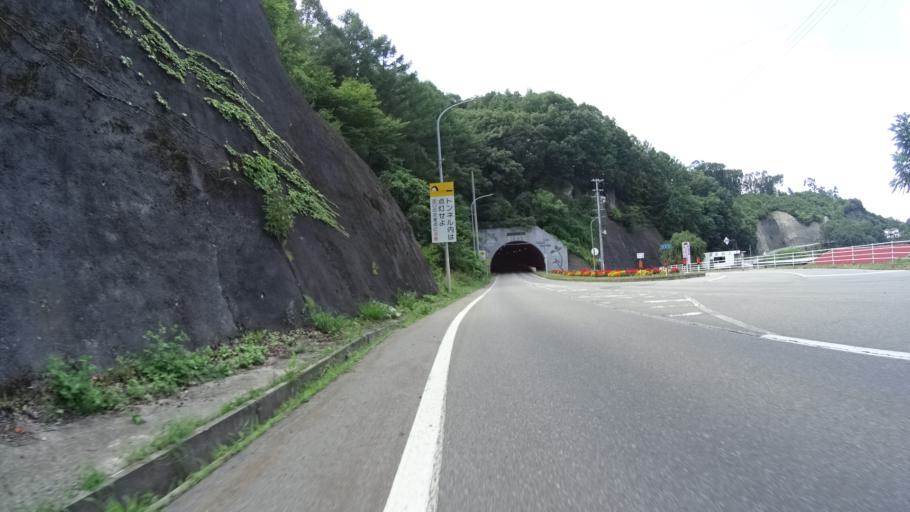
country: JP
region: Nagano
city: Saku
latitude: 36.0822
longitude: 138.4865
